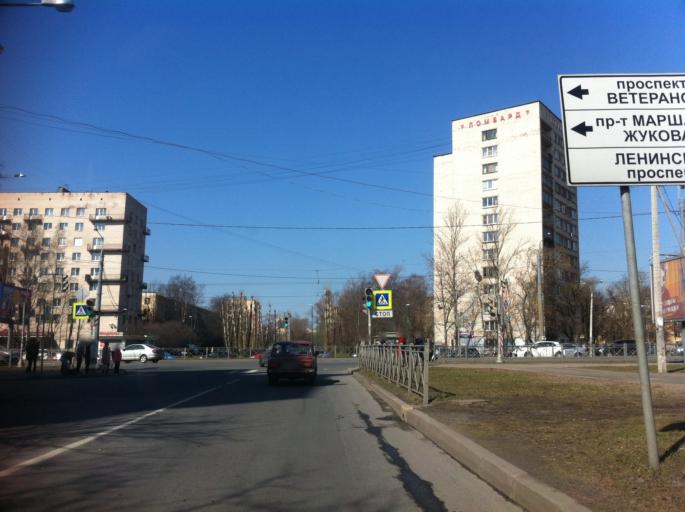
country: RU
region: St.-Petersburg
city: Dachnoye
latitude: 59.8420
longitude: 30.2451
